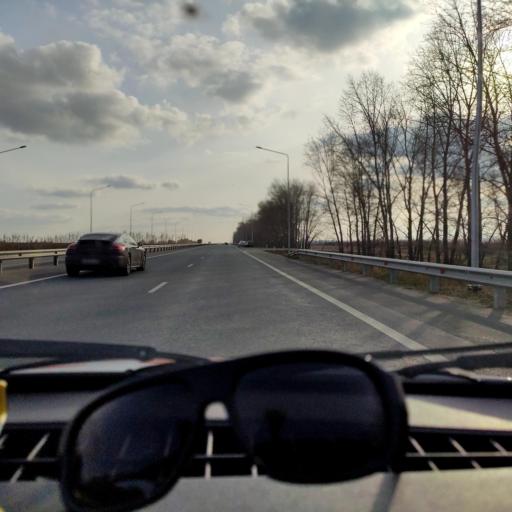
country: RU
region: Bashkortostan
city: Karmaskaly
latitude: 54.3277
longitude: 55.8941
